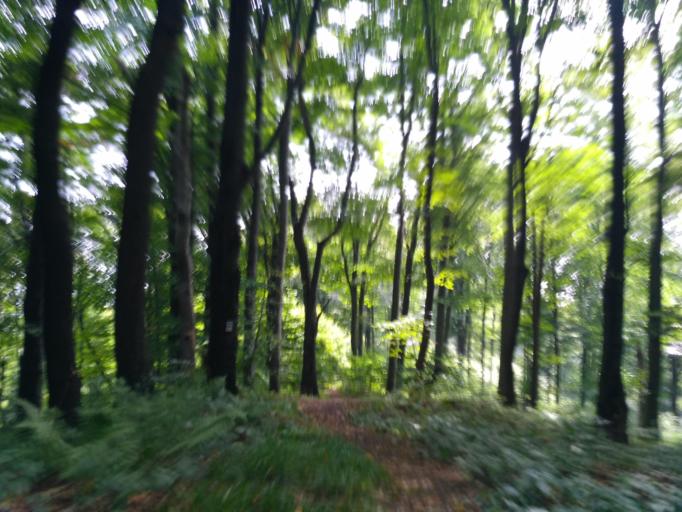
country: PL
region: Subcarpathian Voivodeship
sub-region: Powiat strzyzowski
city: Frysztak
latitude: 49.8884
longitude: 21.5388
